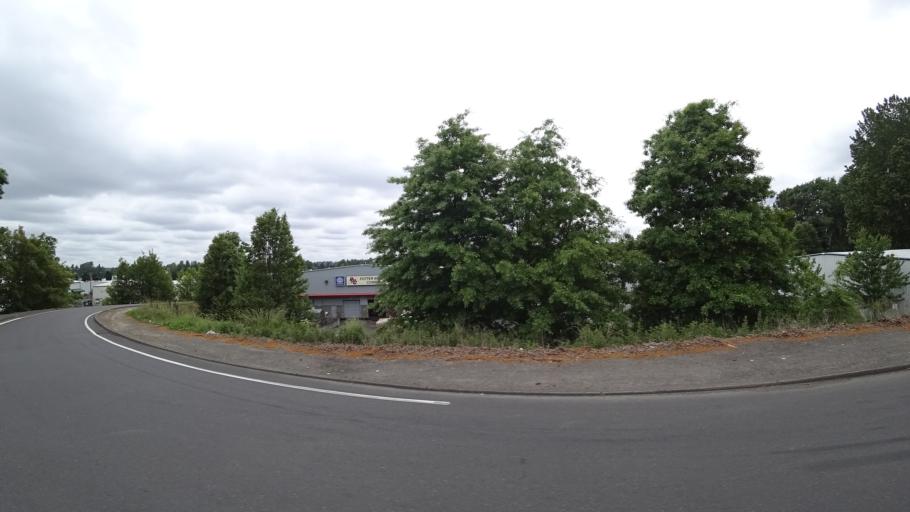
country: US
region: Washington
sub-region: Clark County
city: Vancouver
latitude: 45.5928
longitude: -122.6677
